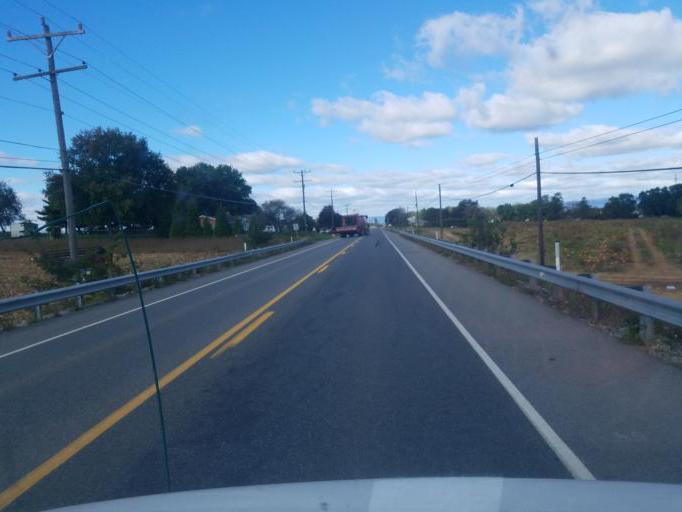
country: US
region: Pennsylvania
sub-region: Franklin County
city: Greencastle
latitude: 39.7834
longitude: -77.6957
